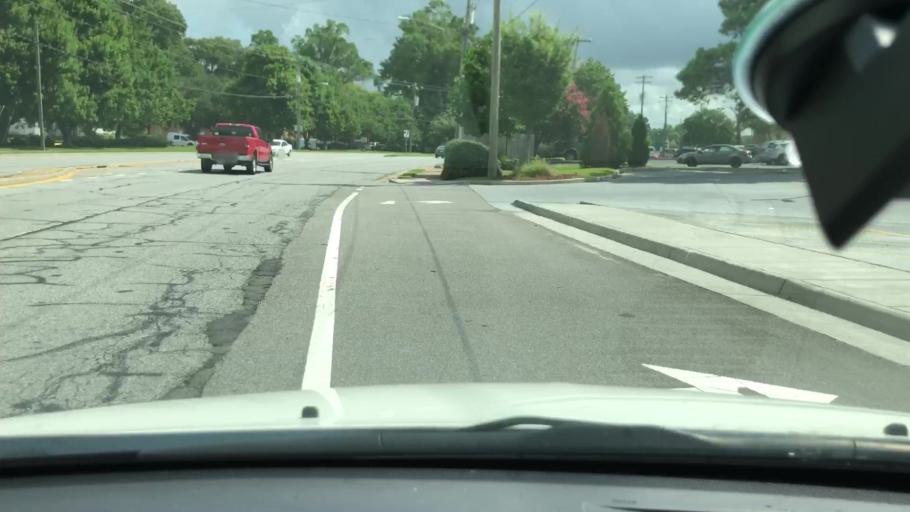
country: US
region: Virginia
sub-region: City of Chesapeake
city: Chesapeake
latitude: 36.8127
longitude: -76.2051
